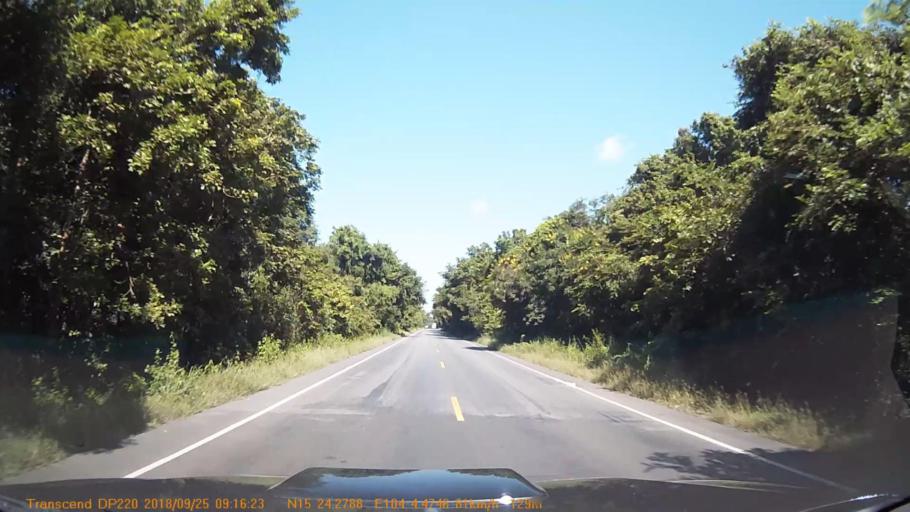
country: TH
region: Sisaket
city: Sila Lat
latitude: 15.4046
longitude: 104.0747
